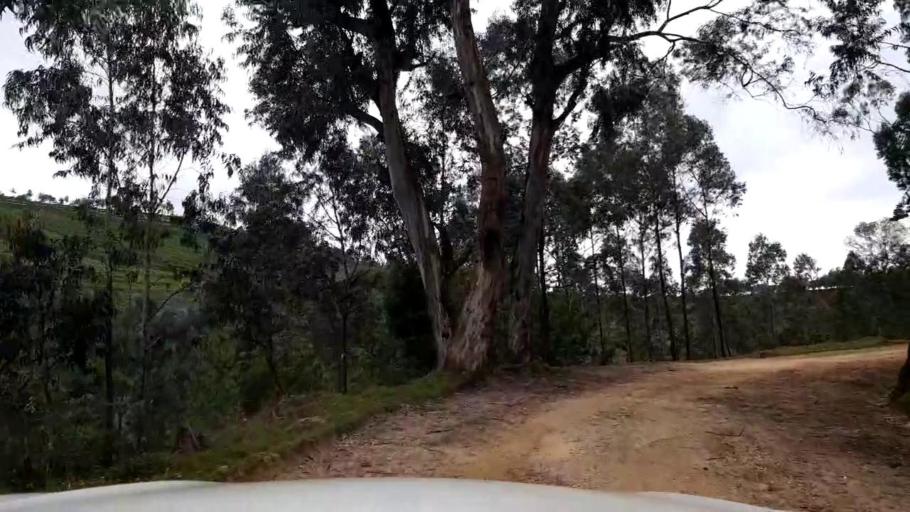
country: RW
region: Western Province
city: Kibuye
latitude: -1.9574
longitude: 29.3989
